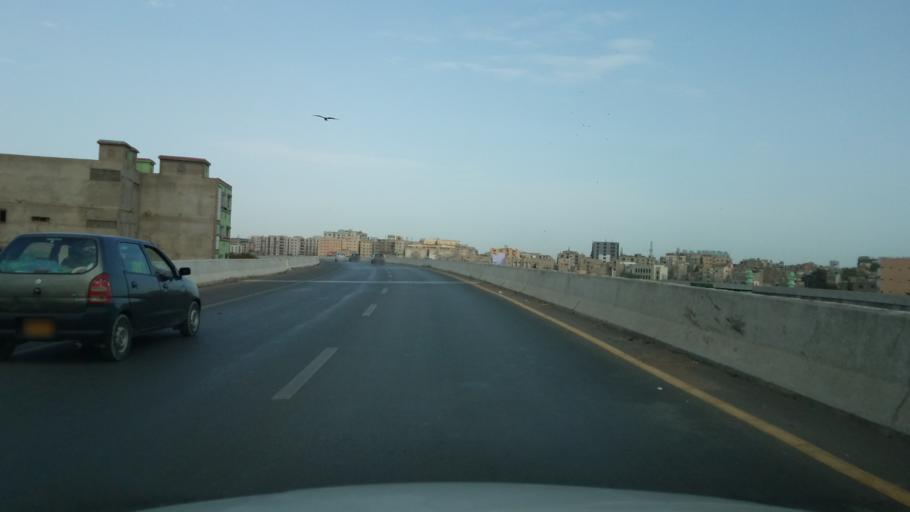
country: PK
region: Sindh
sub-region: Karachi District
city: Karachi
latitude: 24.8795
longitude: 67.0104
